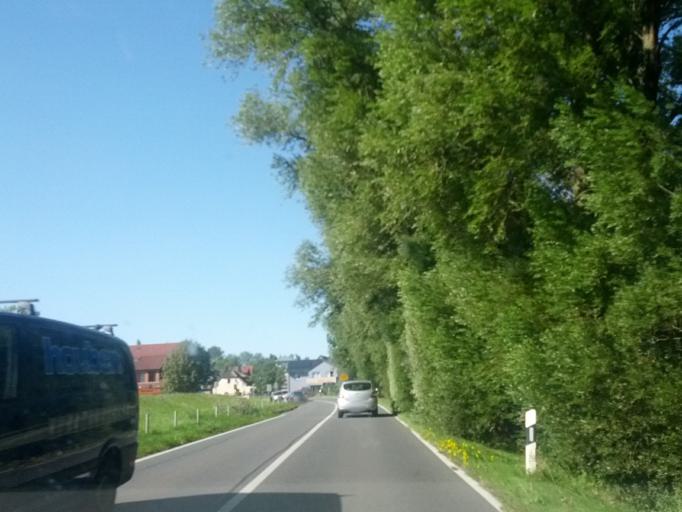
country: DE
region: Mecklenburg-Vorpommern
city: Ostseebad Gohren
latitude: 54.3284
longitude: 13.7057
